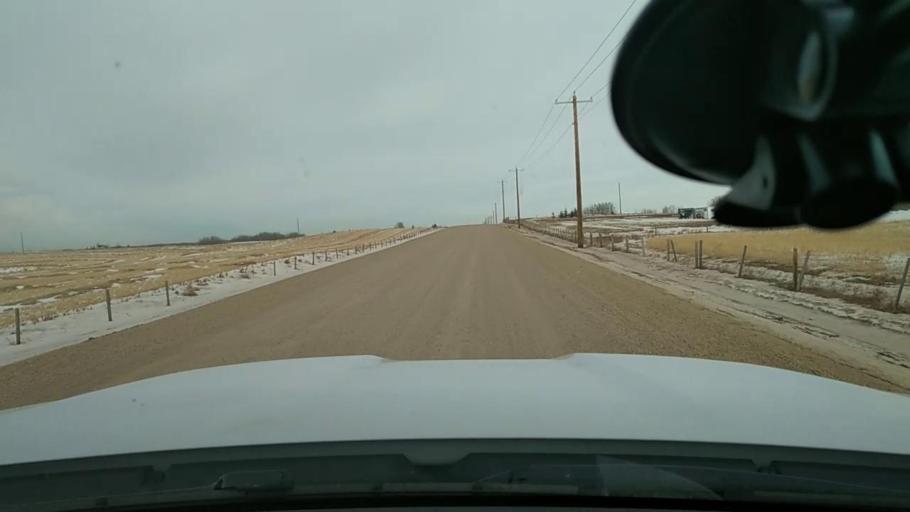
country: CA
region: Alberta
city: Airdrie
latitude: 51.2244
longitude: -113.9118
